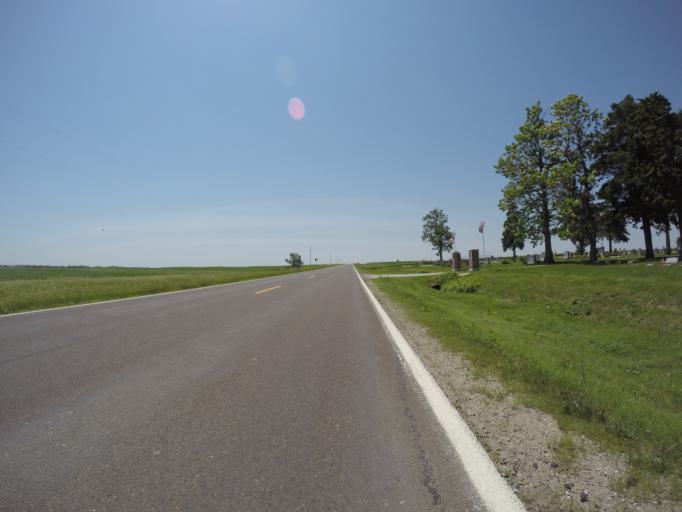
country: US
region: Nebraska
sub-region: Pawnee County
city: Pawnee City
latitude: 40.0233
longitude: -96.0483
